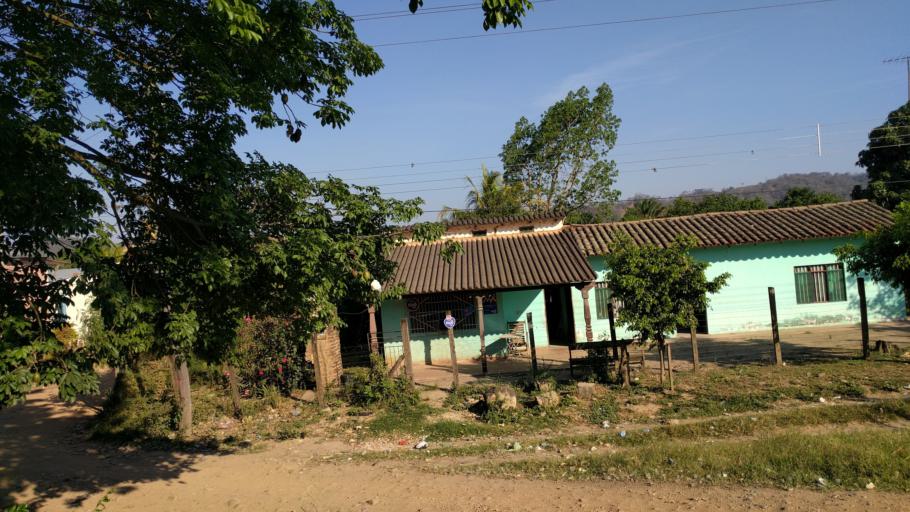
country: BO
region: Santa Cruz
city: Jorochito
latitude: -18.1464
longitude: -63.4841
